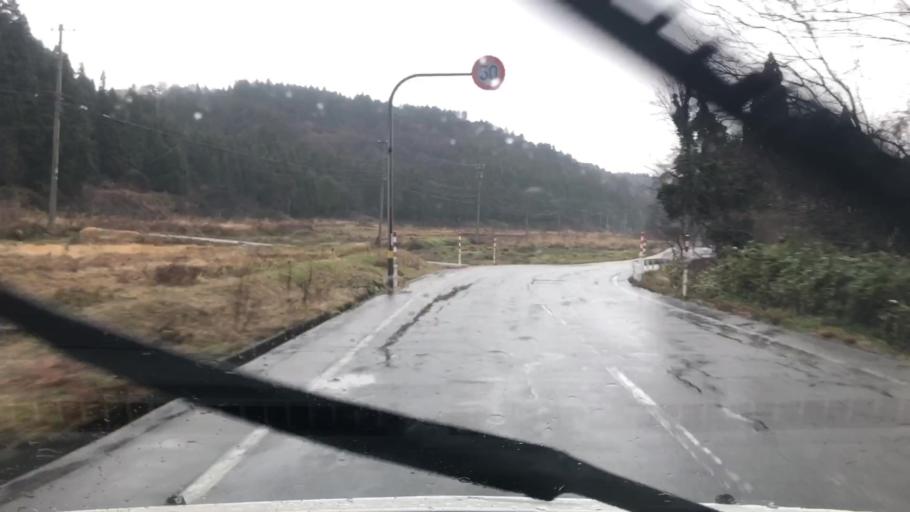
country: JP
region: Toyama
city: Kamiichi
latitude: 36.5860
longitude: 137.3227
